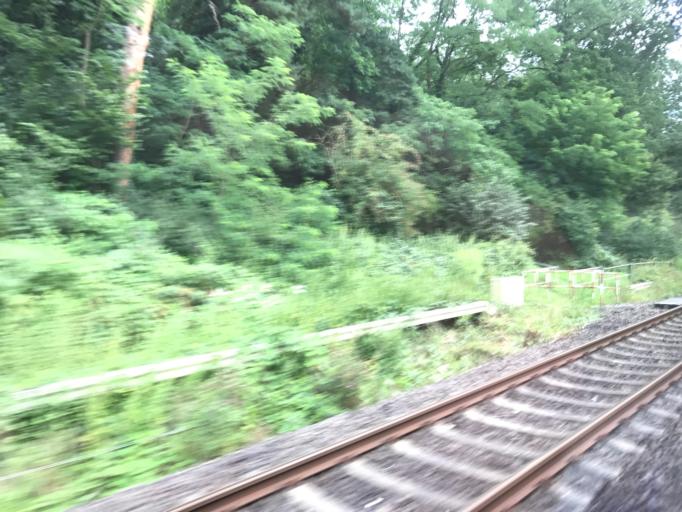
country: DE
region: Hesse
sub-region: Regierungsbezirk Giessen
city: Runkel
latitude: 50.4012
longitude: 8.1660
